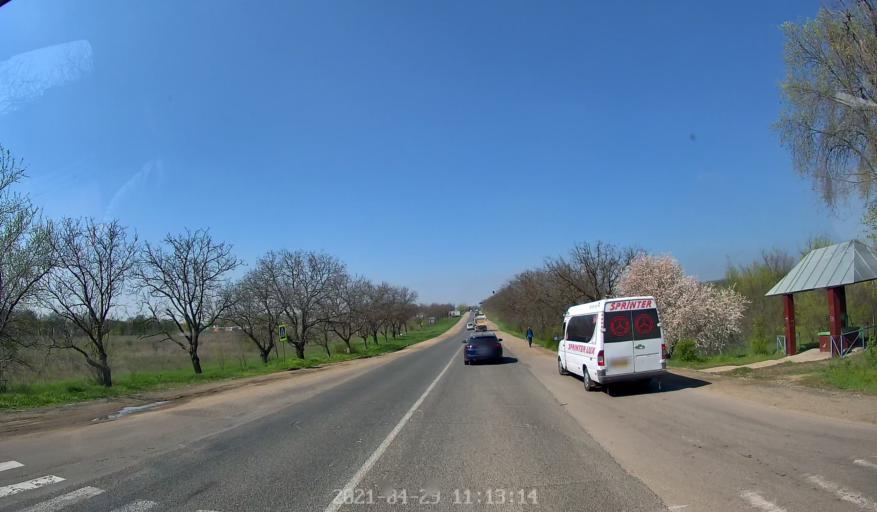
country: MD
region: Chisinau
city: Stauceni
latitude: 47.1177
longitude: 28.8678
